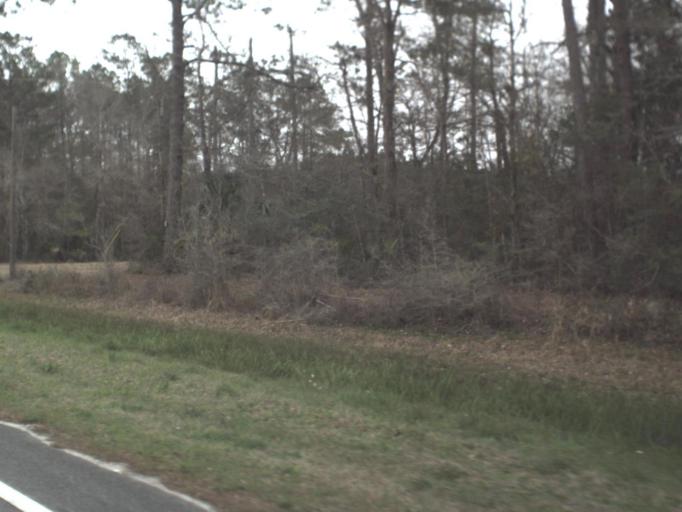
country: US
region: Florida
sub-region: Leon County
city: Woodville
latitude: 30.1873
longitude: -84.2279
